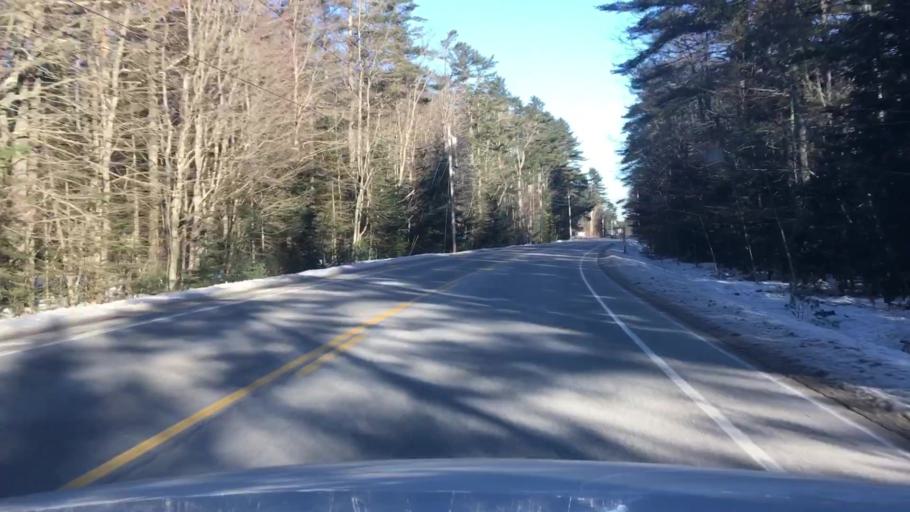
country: US
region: Maine
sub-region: Androscoggin County
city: Lisbon Falls
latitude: 43.9597
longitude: -70.1238
